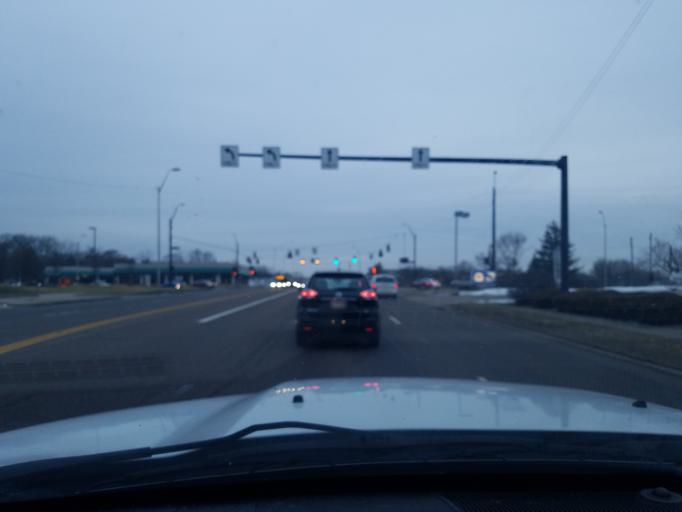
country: US
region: Ohio
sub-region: Montgomery County
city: Kettering
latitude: 39.6883
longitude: -84.1312
